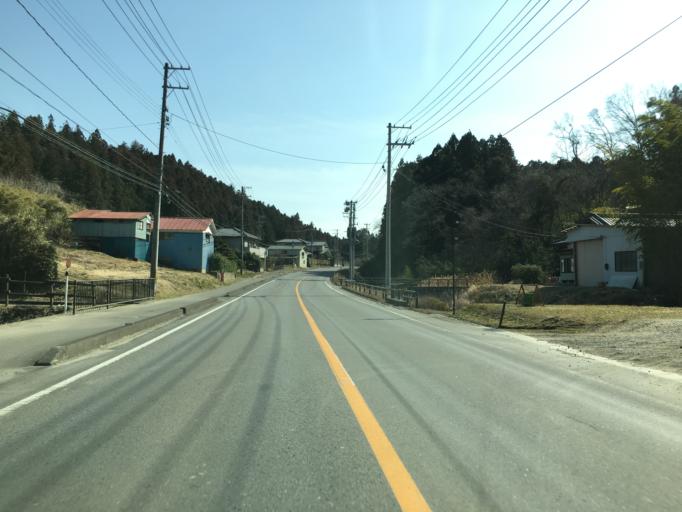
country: JP
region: Ibaraki
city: Daigo
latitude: 36.8592
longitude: 140.4286
